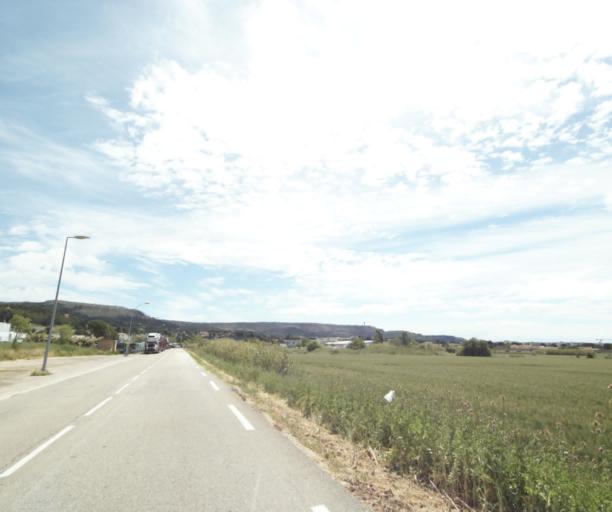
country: FR
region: Provence-Alpes-Cote d'Azur
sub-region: Departement des Bouches-du-Rhone
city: Rognac
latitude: 43.4975
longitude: 5.2242
